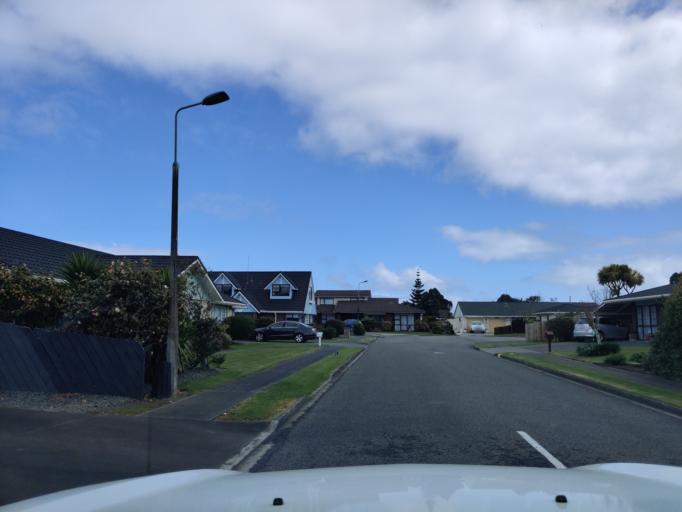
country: NZ
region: Manawatu-Wanganui
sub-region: Wanganui District
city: Wanganui
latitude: -39.9264
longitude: 175.0256
